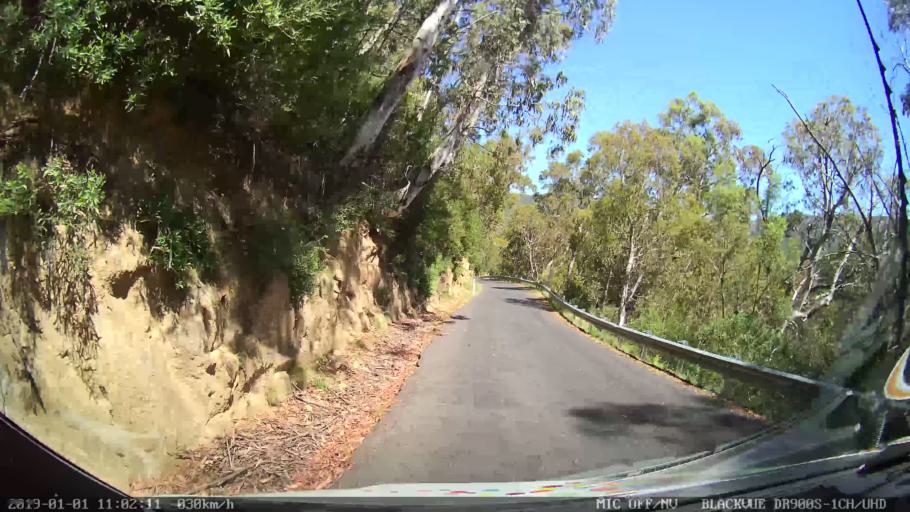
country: AU
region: New South Wales
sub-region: Snowy River
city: Jindabyne
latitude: -35.9738
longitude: 148.3985
